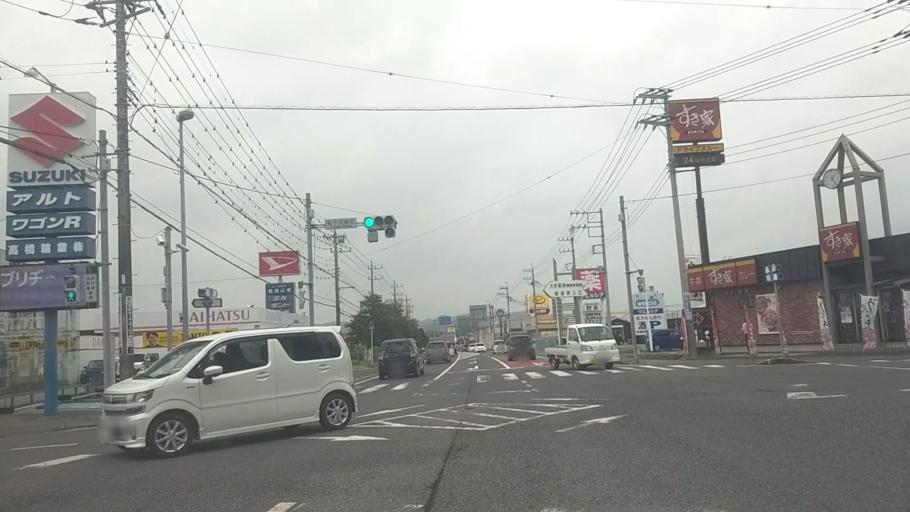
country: JP
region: Chiba
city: Ohara
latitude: 35.2859
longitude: 140.2525
